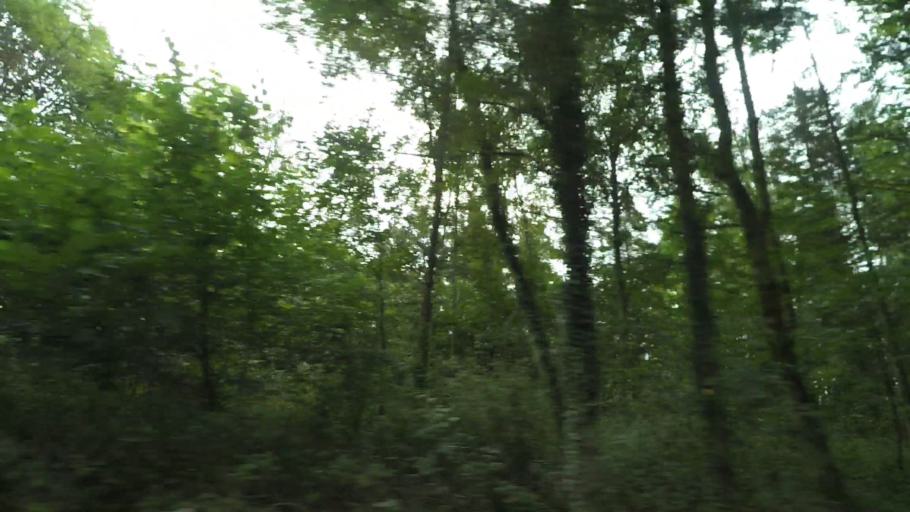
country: DK
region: Central Jutland
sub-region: Syddjurs Kommune
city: Ryomgard
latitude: 56.3435
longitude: 10.4887
